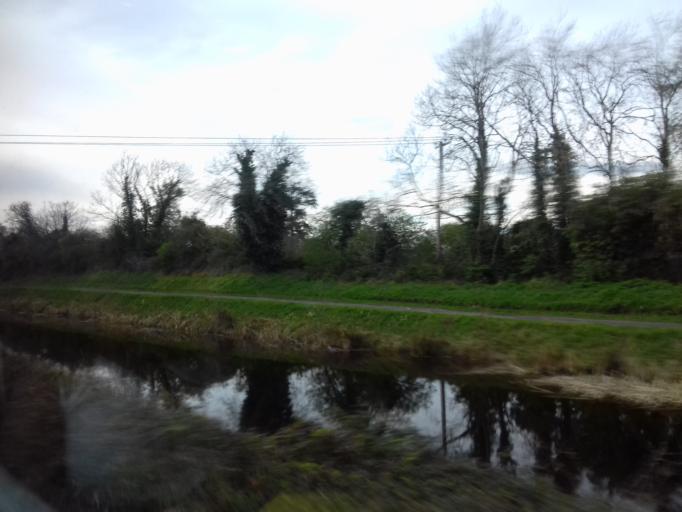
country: IE
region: Leinster
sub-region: Kildare
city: Maynooth
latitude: 53.3794
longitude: -6.5705
